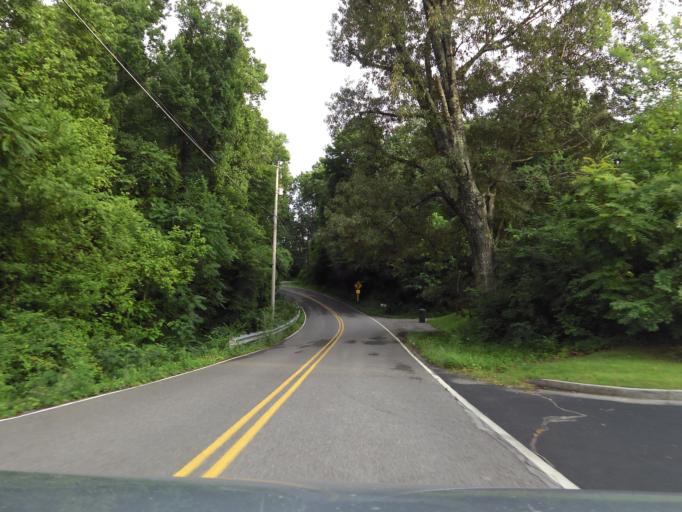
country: US
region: Tennessee
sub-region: Knox County
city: Knoxville
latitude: 35.9358
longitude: -83.9273
